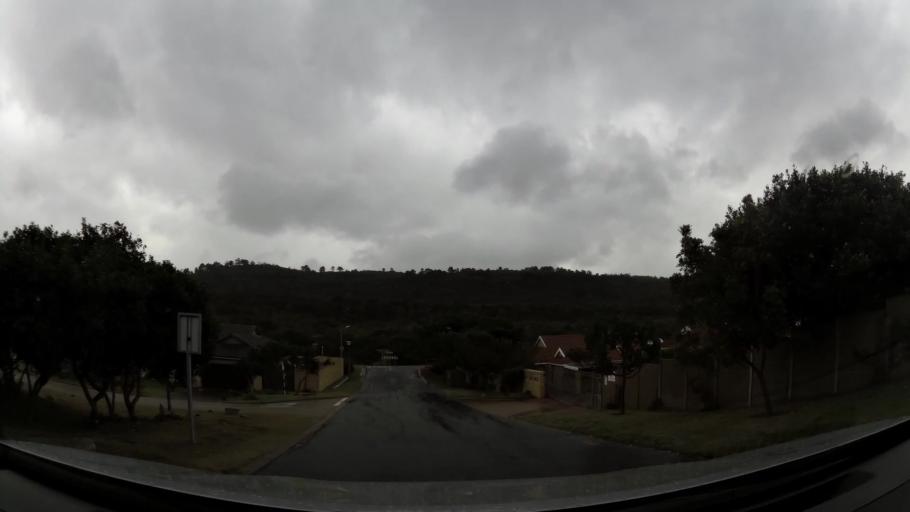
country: ZA
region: Western Cape
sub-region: Eden District Municipality
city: Mossel Bay
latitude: -34.0527
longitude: 22.2556
